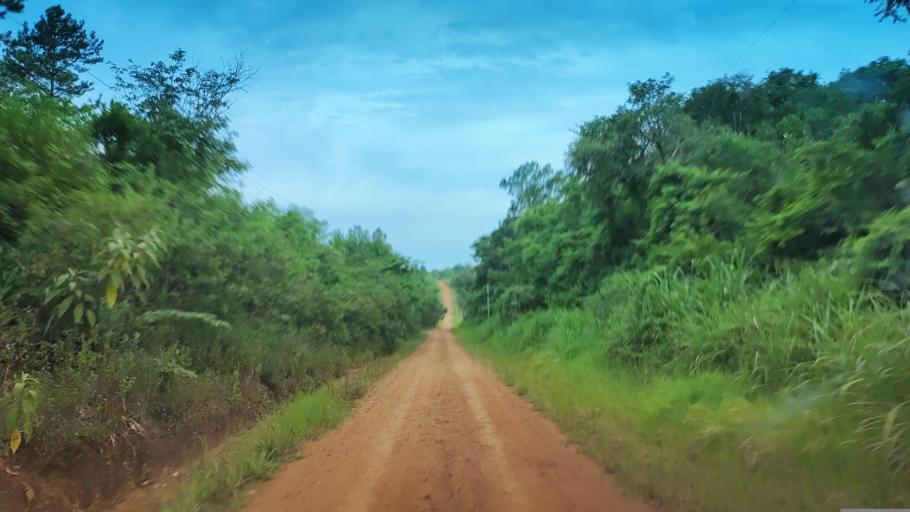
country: AR
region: Misiones
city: Gobernador Roca
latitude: -27.1559
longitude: -55.4662
